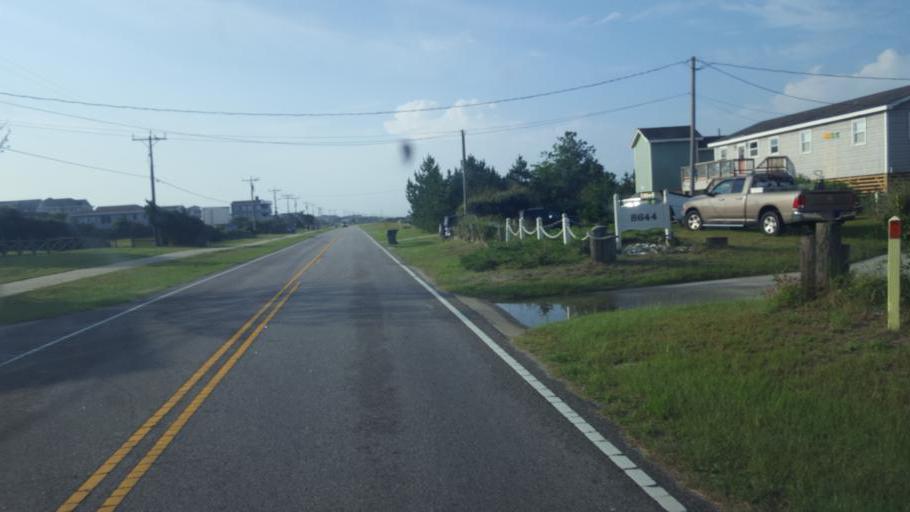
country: US
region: North Carolina
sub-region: Dare County
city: Wanchese
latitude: 35.8895
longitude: -75.5868
